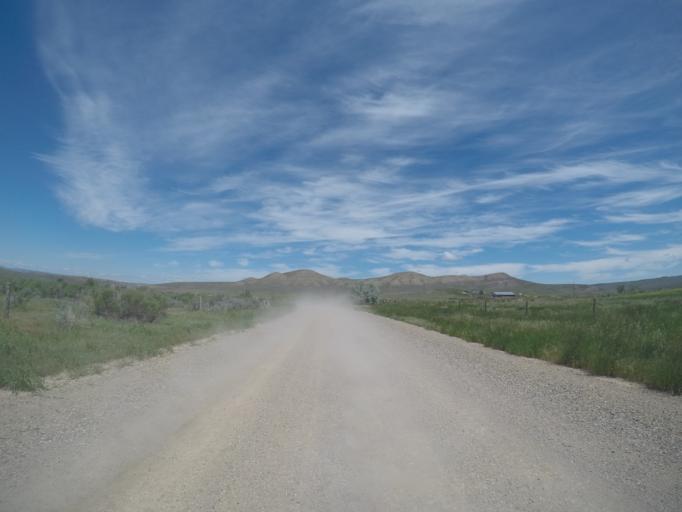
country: US
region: Montana
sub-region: Carbon County
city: Red Lodge
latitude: 45.2279
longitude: -108.8428
